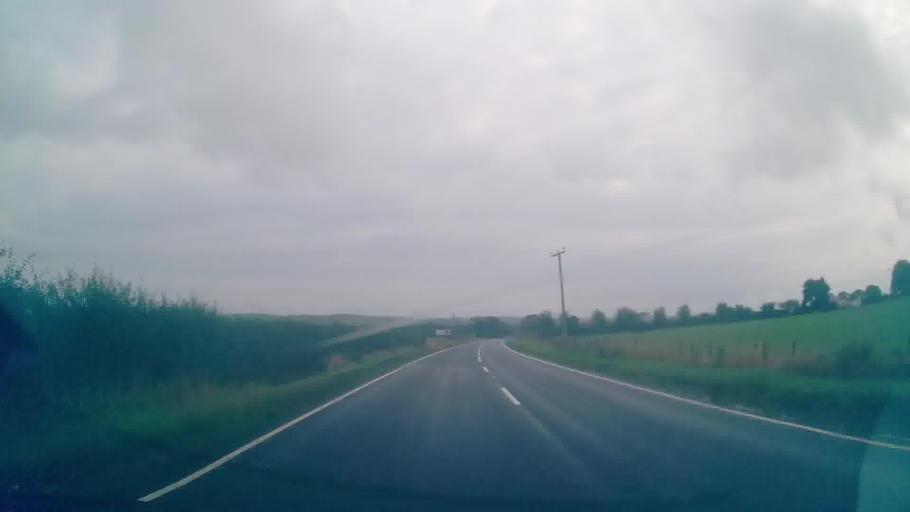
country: GB
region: Scotland
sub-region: Dumfries and Galloway
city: Locharbriggs
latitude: 55.0688
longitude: -3.5405
